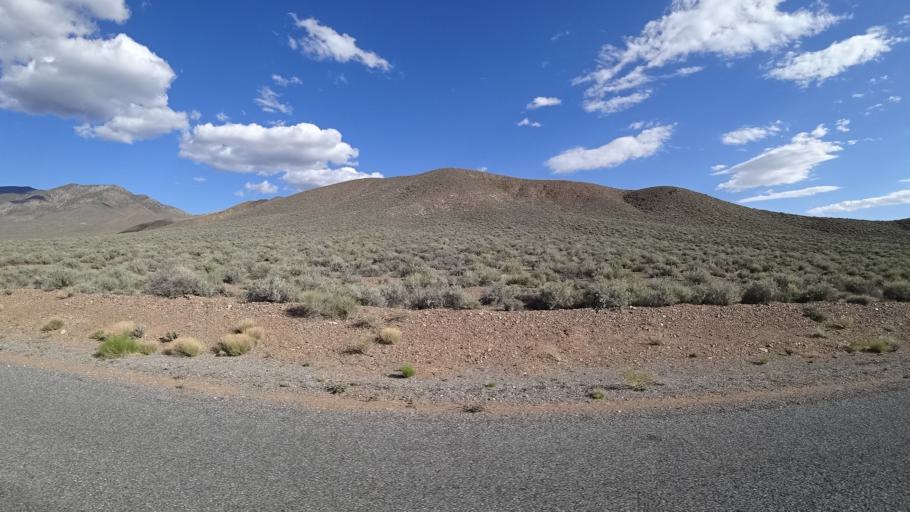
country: US
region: California
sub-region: San Bernardino County
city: Searles Valley
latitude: 36.3009
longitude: -117.1683
